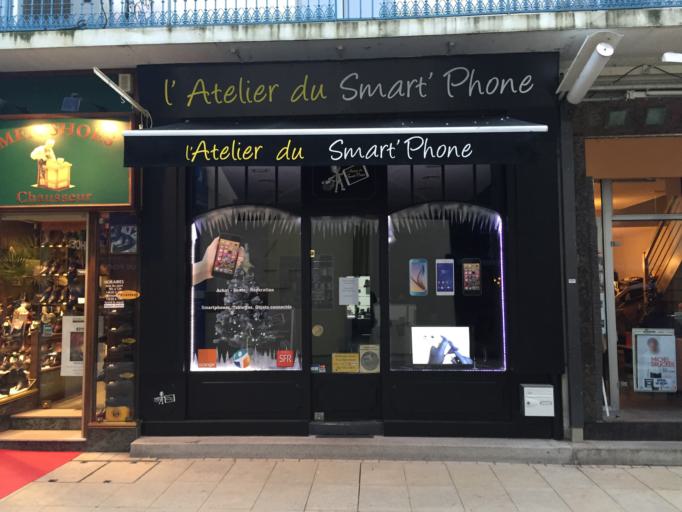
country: FR
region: Auvergne
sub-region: Departement de l'Allier
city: Vichy
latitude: 46.1249
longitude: 3.4221
